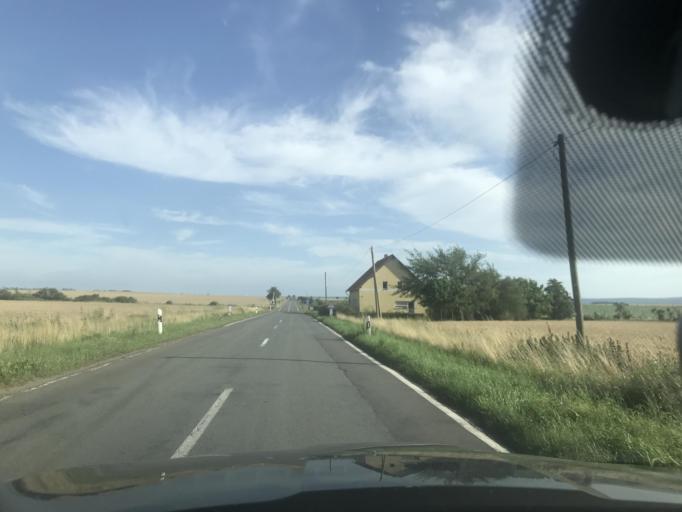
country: DE
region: Saxony-Anhalt
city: Wegeleben
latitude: 51.8657
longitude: 11.1833
